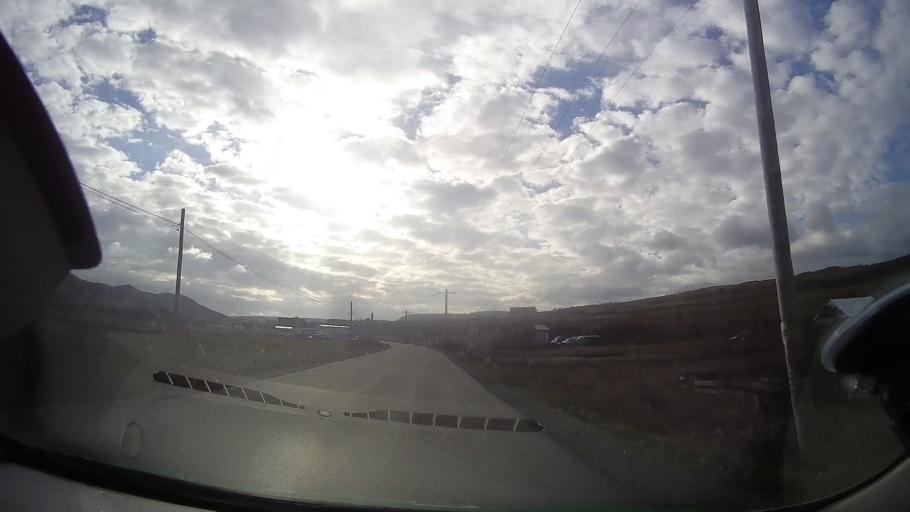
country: RO
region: Cluj
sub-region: Comuna Floresti
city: Luna de Sus
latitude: 46.7226
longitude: 23.4214
